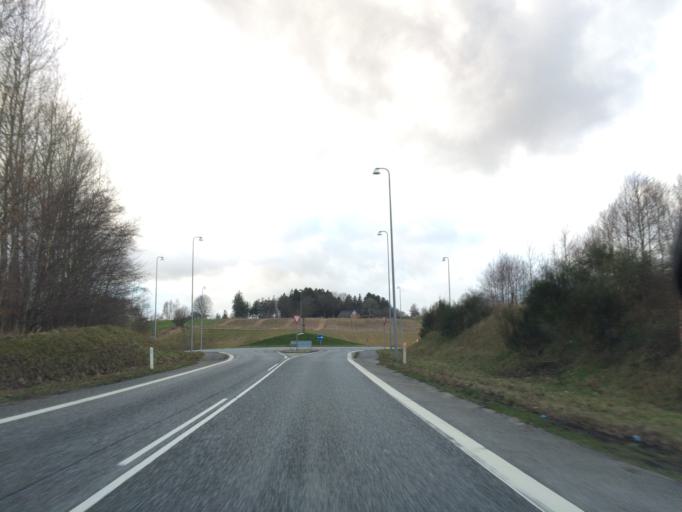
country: DK
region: Central Jutland
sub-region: Silkeborg Kommune
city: Virklund
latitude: 56.1053
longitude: 9.5764
